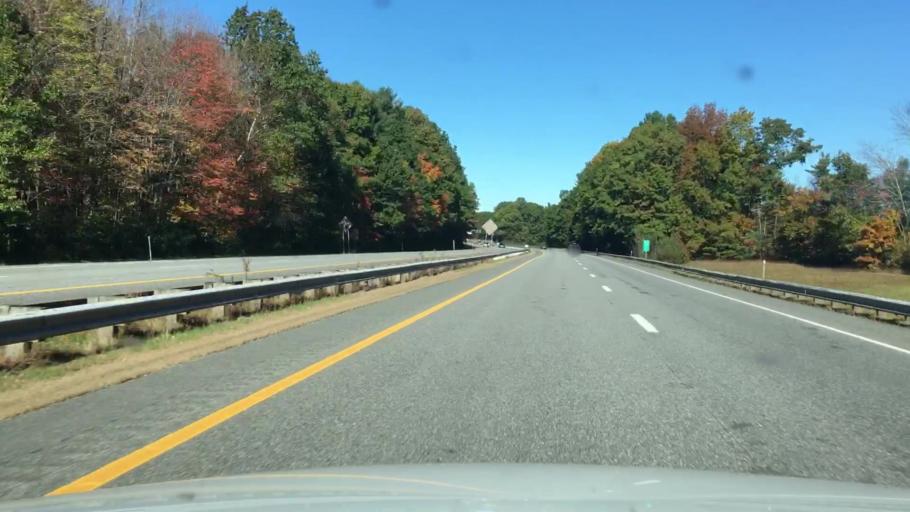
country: US
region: Maine
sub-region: York County
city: Eliot
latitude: 43.1567
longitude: -70.8482
